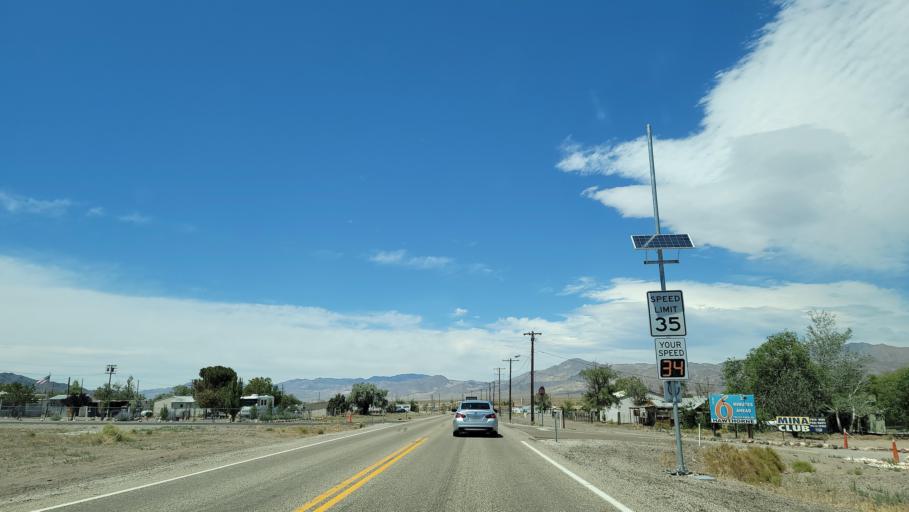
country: US
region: Nevada
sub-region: Mineral County
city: Hawthorne
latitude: 38.3842
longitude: -118.1068
